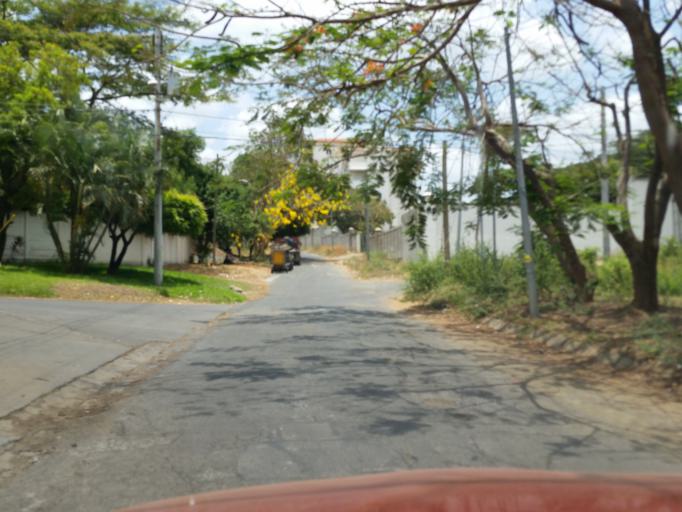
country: NI
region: Managua
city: Managua
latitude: 12.0979
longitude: -86.2459
